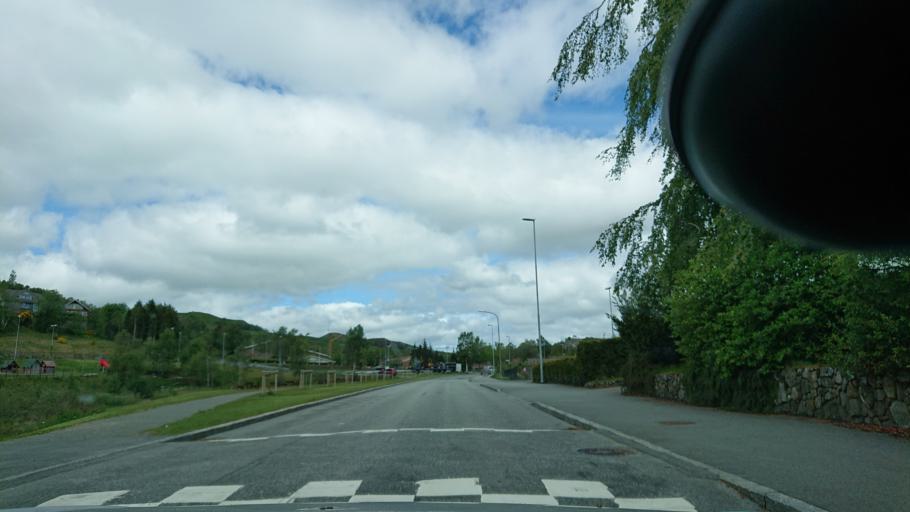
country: NO
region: Rogaland
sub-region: Gjesdal
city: Algard
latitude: 58.7707
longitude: 5.8651
